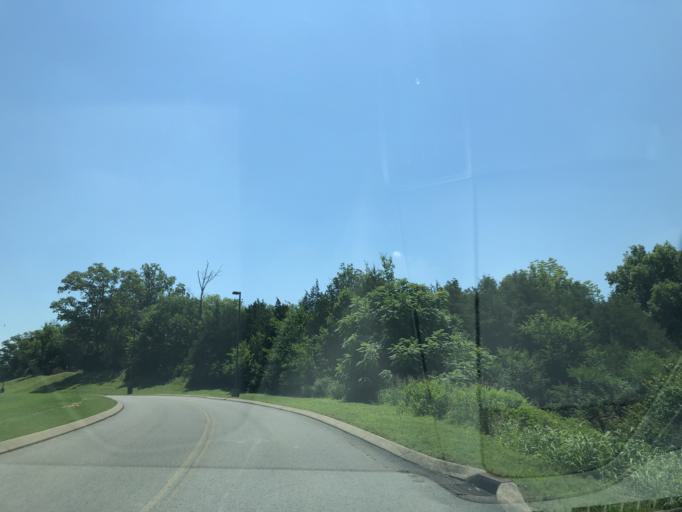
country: US
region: Tennessee
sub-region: Williamson County
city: Nolensville
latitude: 36.0214
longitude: -86.6616
